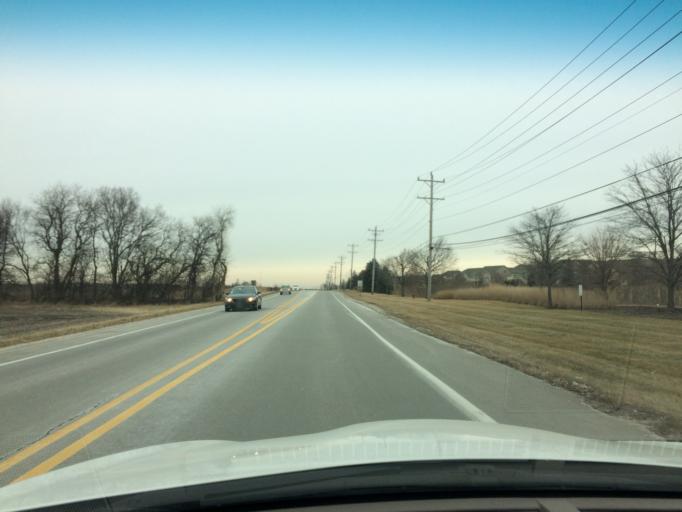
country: US
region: Illinois
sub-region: Kane County
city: Geneva
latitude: 41.8929
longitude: -88.3597
